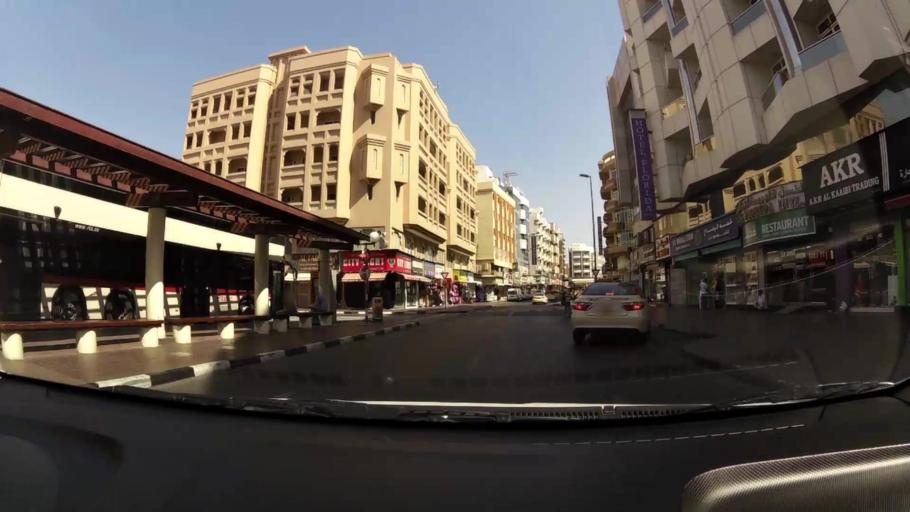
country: AE
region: Ash Shariqah
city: Sharjah
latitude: 25.2699
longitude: 55.3030
